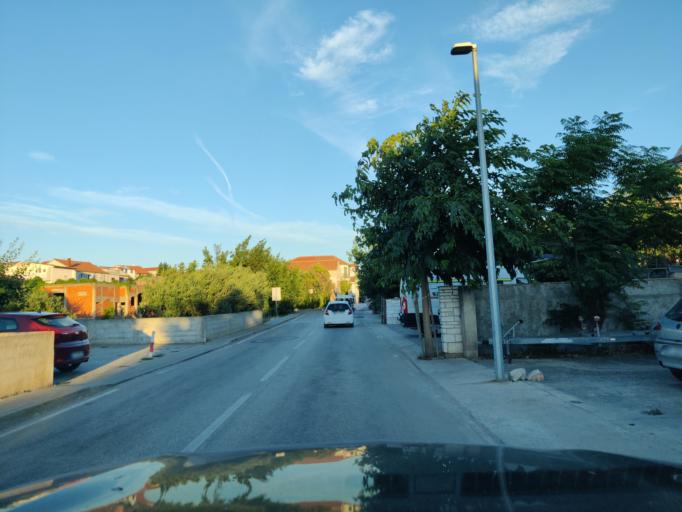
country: HR
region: Sibensko-Kniniska
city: Murter
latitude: 43.8242
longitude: 15.6019
